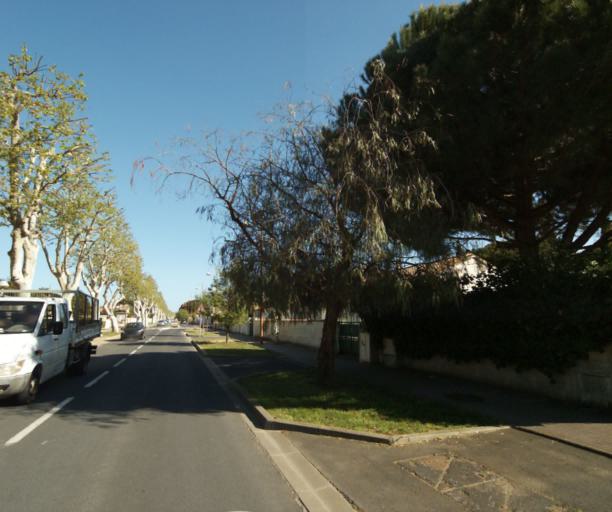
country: FR
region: Languedoc-Roussillon
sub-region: Departement de l'Herault
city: Perols
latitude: 43.5694
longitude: 3.9447
